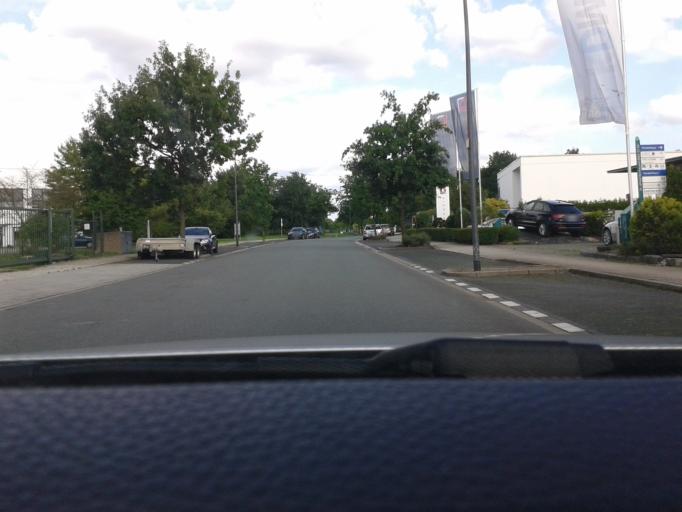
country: DE
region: North Rhine-Westphalia
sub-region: Regierungsbezirk Dusseldorf
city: Hochfeld
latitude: 51.4288
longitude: 6.6946
